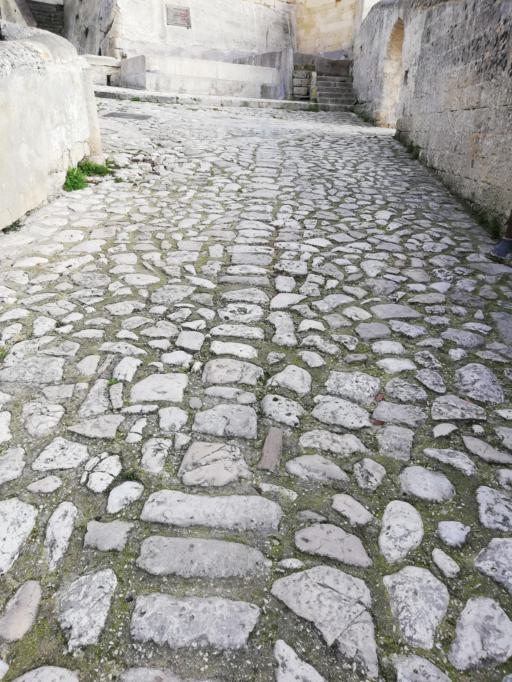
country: IT
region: Apulia
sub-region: Provincia di Bari
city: Gravina in Puglia
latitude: 40.8200
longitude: 16.4135
